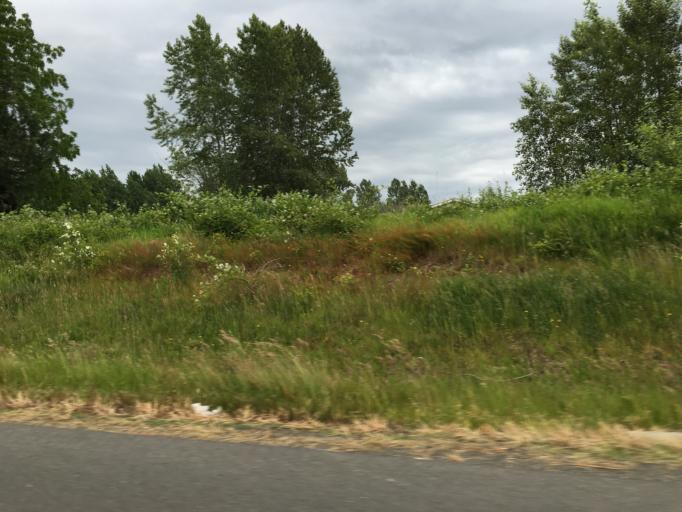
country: US
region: Washington
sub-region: Whatcom County
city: Bellingham
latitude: 48.8252
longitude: -122.4858
